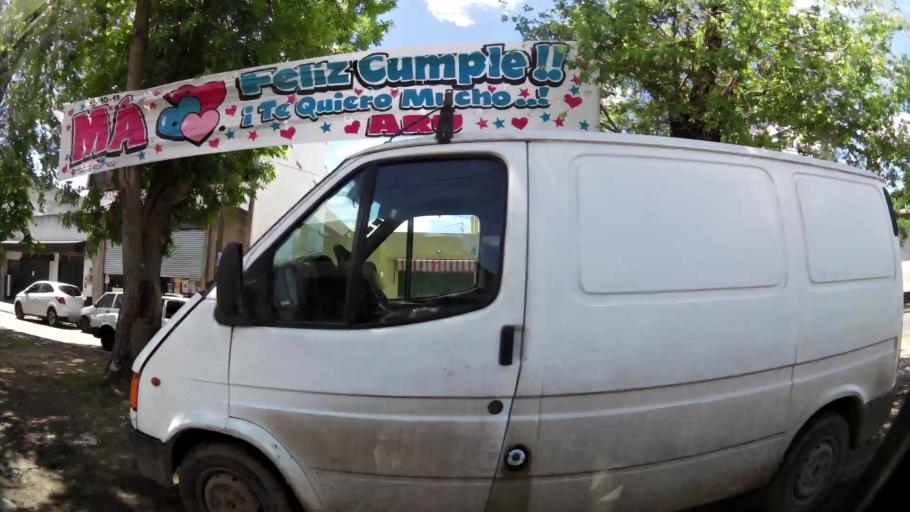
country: AR
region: Buenos Aires
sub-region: Partido de Lanus
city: Lanus
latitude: -34.7253
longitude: -58.4074
